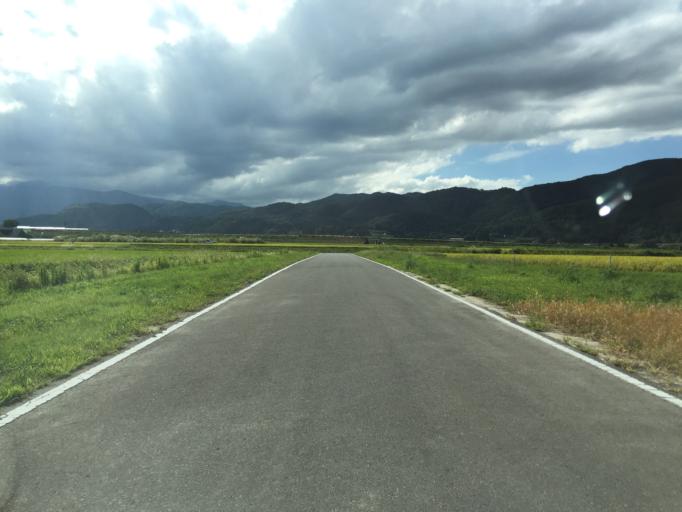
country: JP
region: Fukushima
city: Fukushima-shi
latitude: 37.8027
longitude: 140.4182
